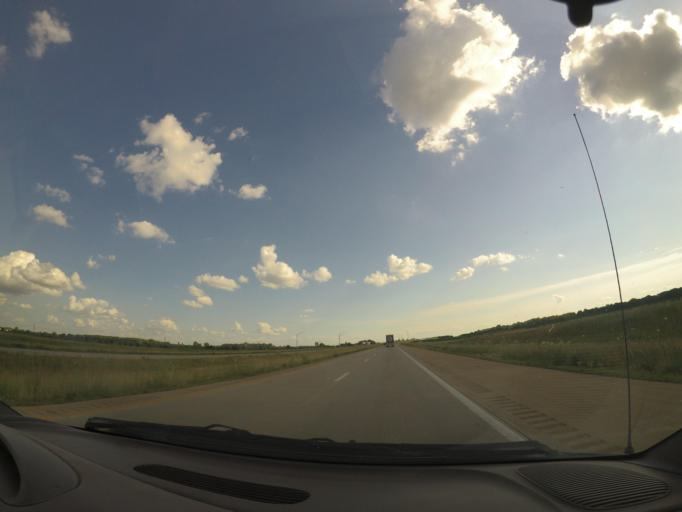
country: US
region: Ohio
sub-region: Lucas County
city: Waterville
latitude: 41.5075
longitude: -83.7551
